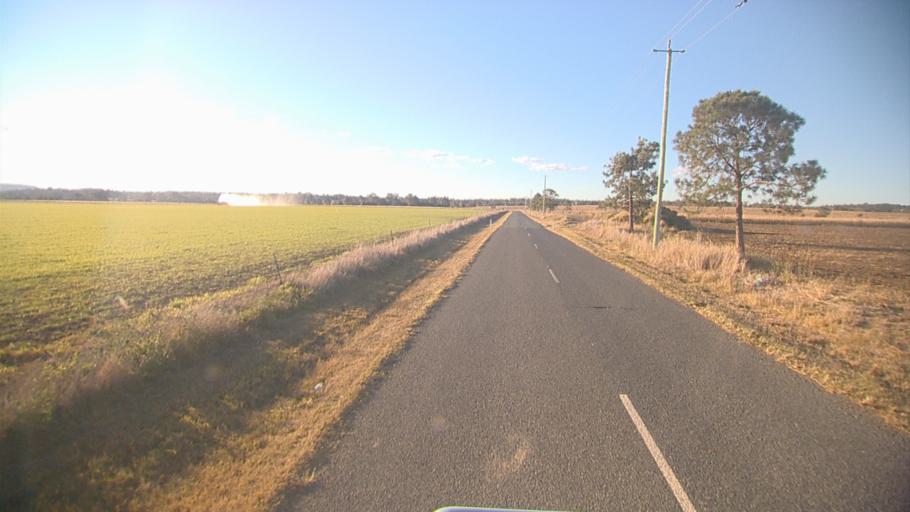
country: AU
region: Queensland
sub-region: Logan
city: Cedar Vale
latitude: -27.8562
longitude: 152.9599
